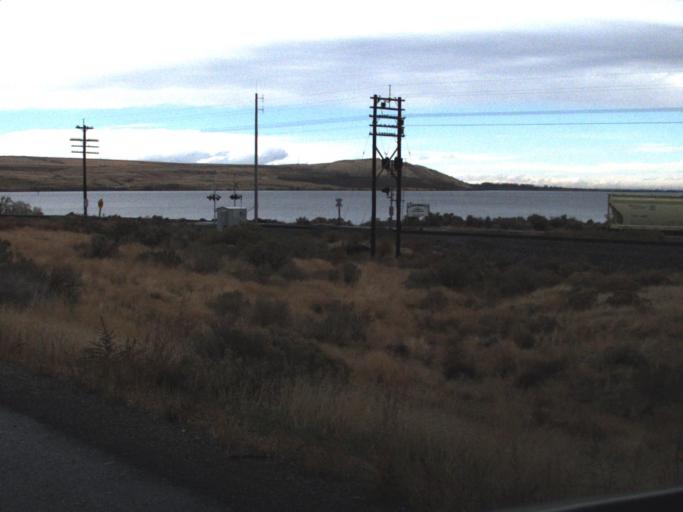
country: US
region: Washington
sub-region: Benton County
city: Finley
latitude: 46.0568
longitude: -118.9215
